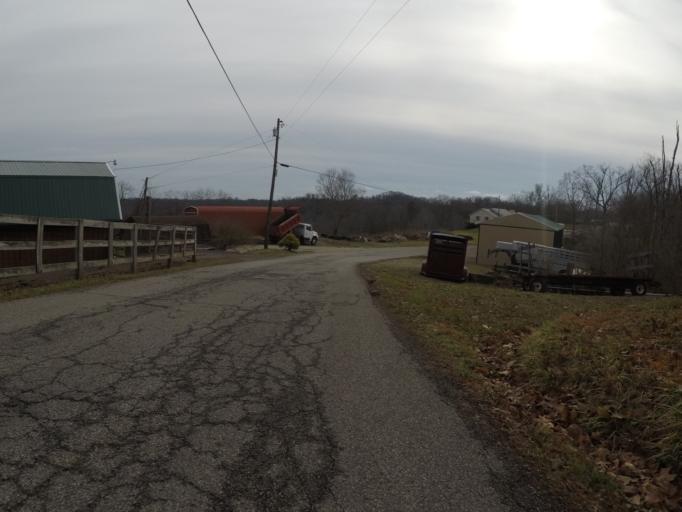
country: US
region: West Virginia
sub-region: Wayne County
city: Lavalette
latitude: 38.3620
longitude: -82.4122
